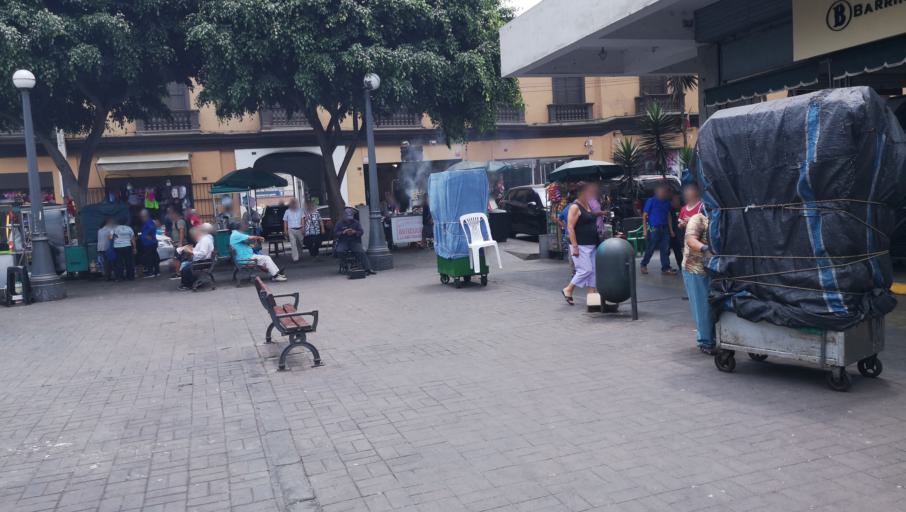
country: PE
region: Lima
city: Lima
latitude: -12.0495
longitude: -77.0264
